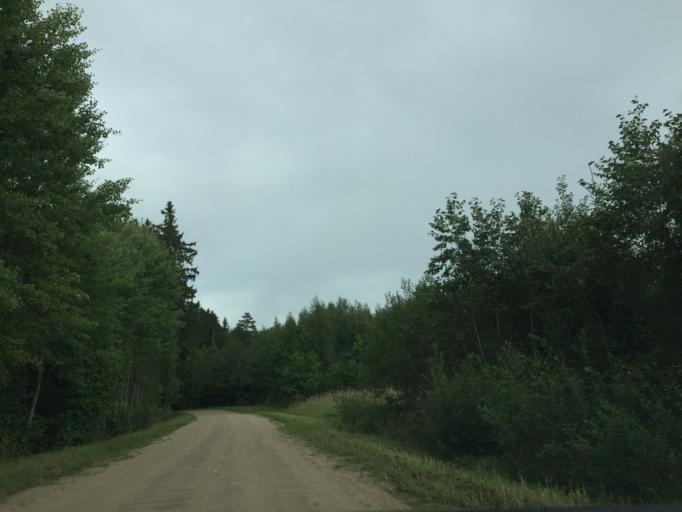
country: LV
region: Pargaujas
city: Stalbe
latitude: 57.5199
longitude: 24.9155
